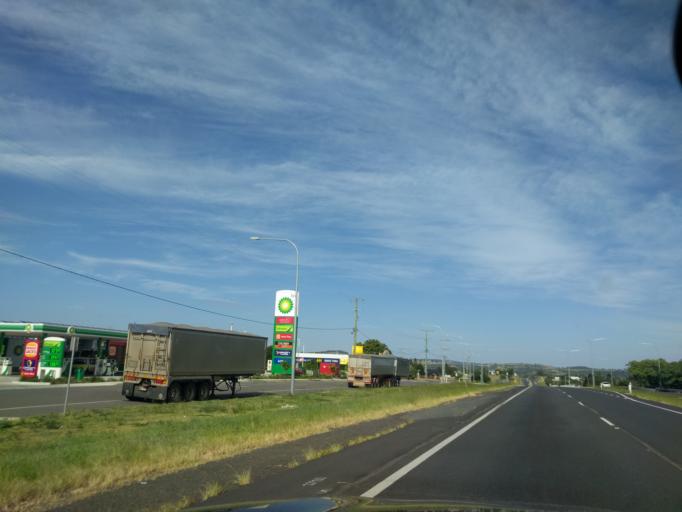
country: AU
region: Queensland
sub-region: Ipswich
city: Thagoona
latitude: -27.5684
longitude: 152.6235
